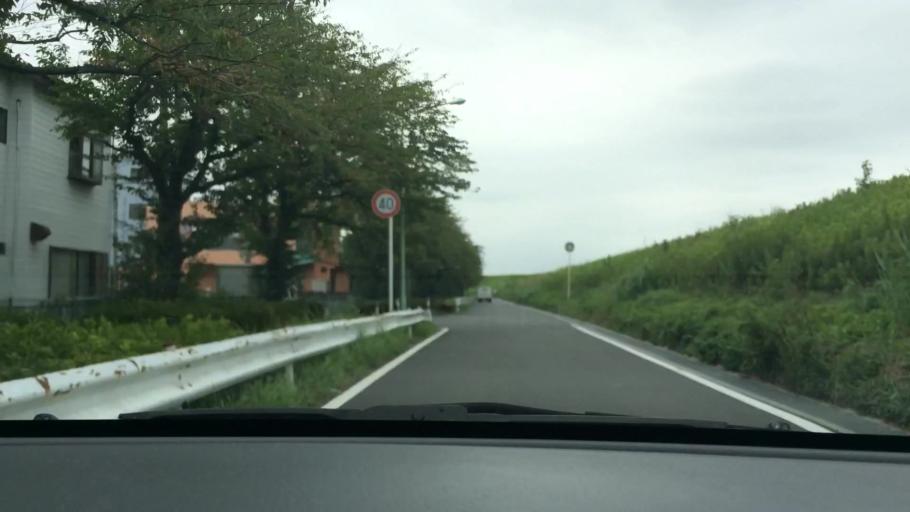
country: JP
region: Chiba
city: Matsudo
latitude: 35.8109
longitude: 139.8855
